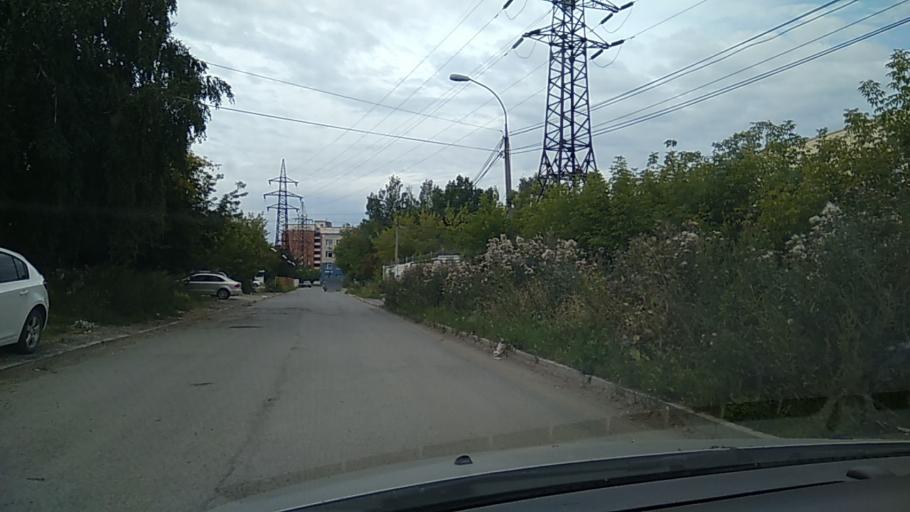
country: RU
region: Sverdlovsk
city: Yekaterinburg
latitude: 56.8825
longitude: 60.6218
